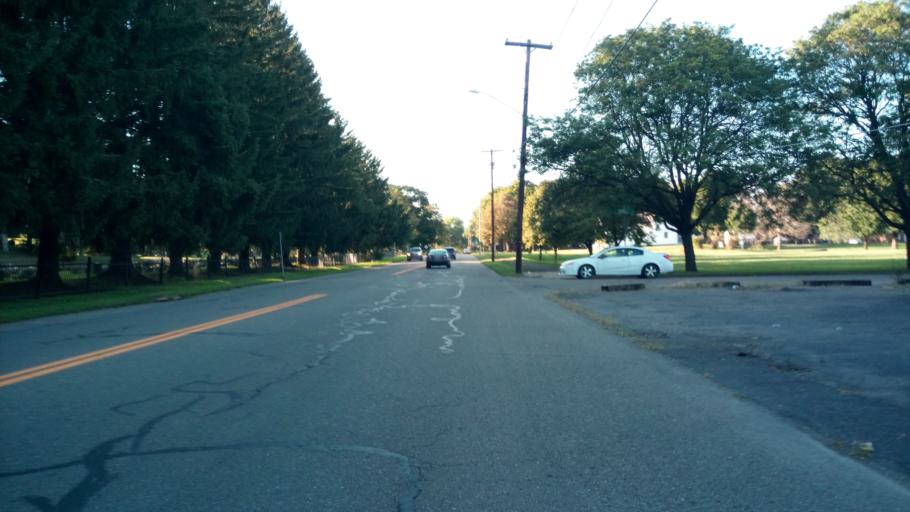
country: US
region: New York
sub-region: Chemung County
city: Elmira Heights
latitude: 42.1067
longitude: -76.8242
